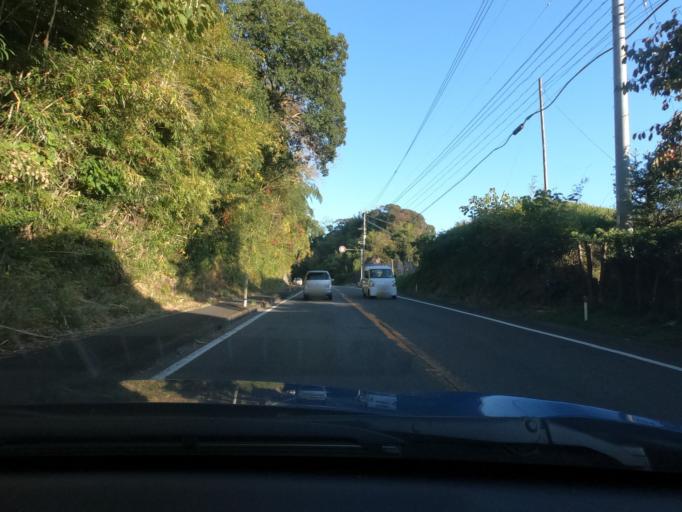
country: JP
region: Kagoshima
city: Satsumasendai
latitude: 31.8472
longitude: 130.2532
